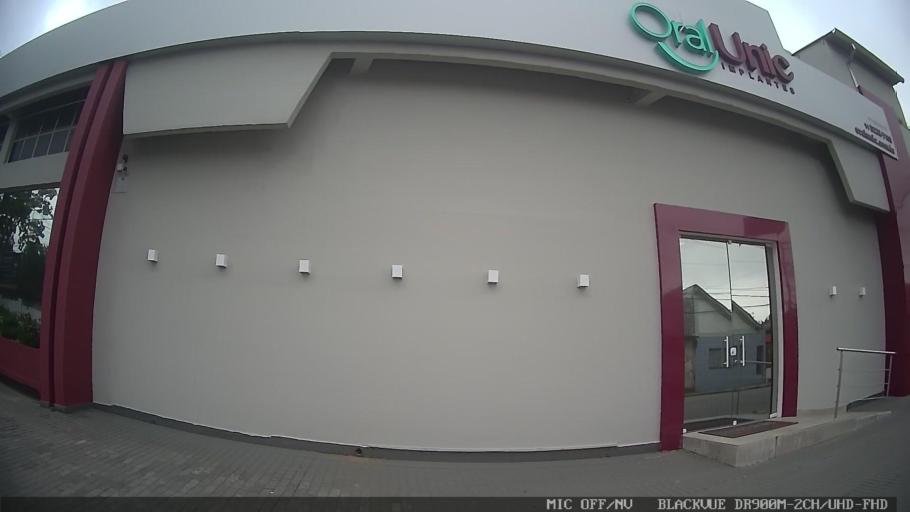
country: BR
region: Sao Paulo
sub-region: Mogi das Cruzes
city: Mogi das Cruzes
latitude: -23.5178
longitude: -46.2012
